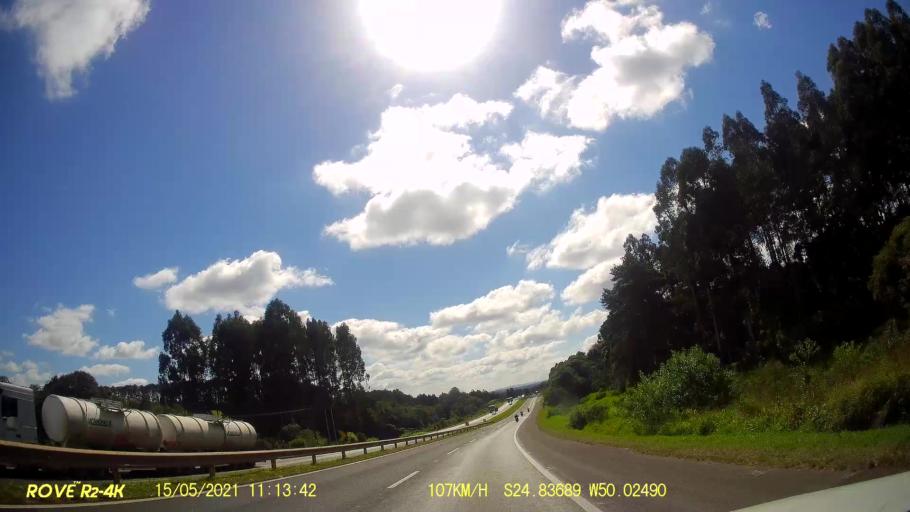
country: BR
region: Parana
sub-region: Castro
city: Castro
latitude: -24.8369
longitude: -50.0248
